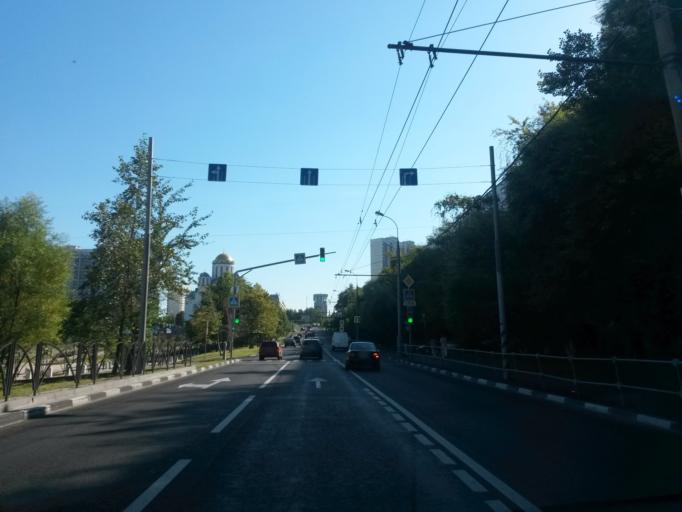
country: RU
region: Moscow
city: Yasenevo
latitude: 55.6175
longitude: 37.5407
